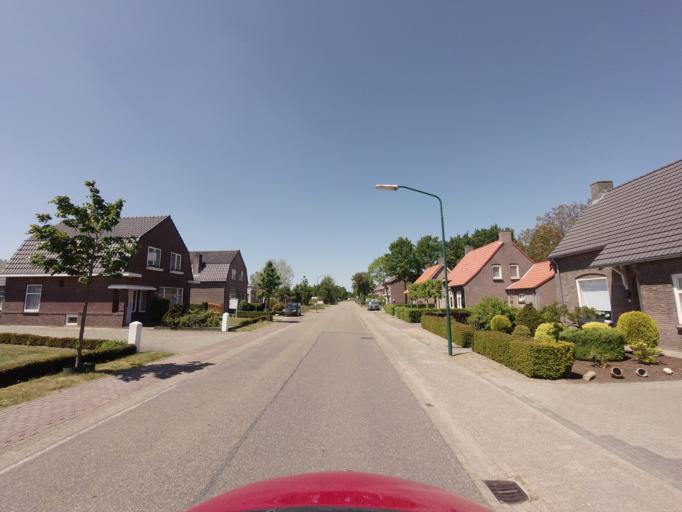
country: NL
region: North Brabant
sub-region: Bergeijk
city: Bergeyk
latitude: 51.2906
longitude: 5.3186
